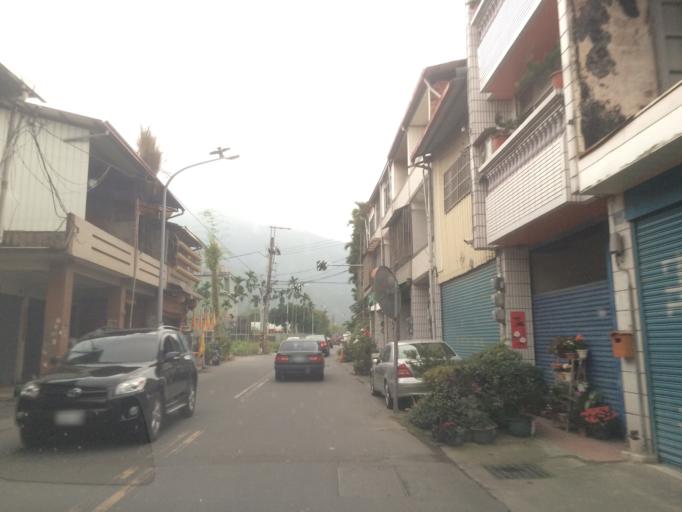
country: TW
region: Taiwan
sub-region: Nantou
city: Puli
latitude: 23.9523
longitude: 120.9812
